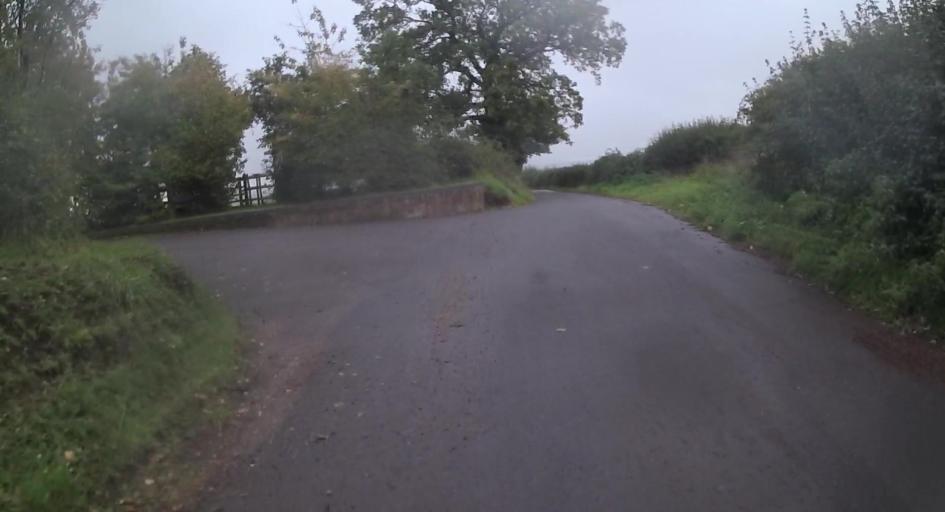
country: GB
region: England
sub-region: West Berkshire
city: Thatcham
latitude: 51.4098
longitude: -1.2137
